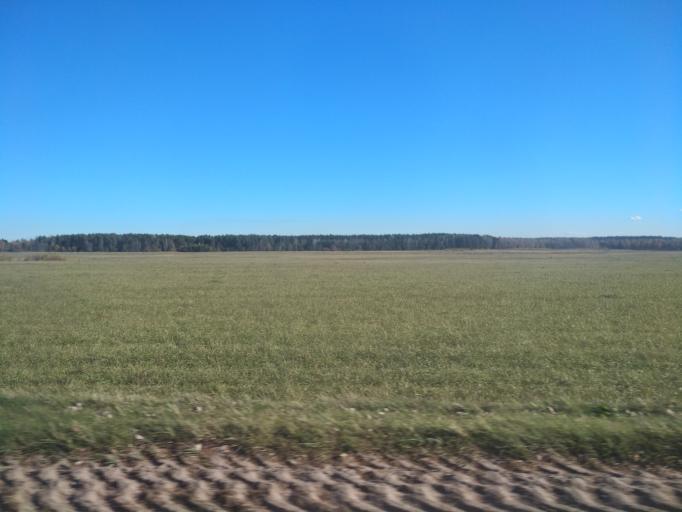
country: BY
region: Minsk
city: Il'ya
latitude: 54.5567
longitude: 27.2134
